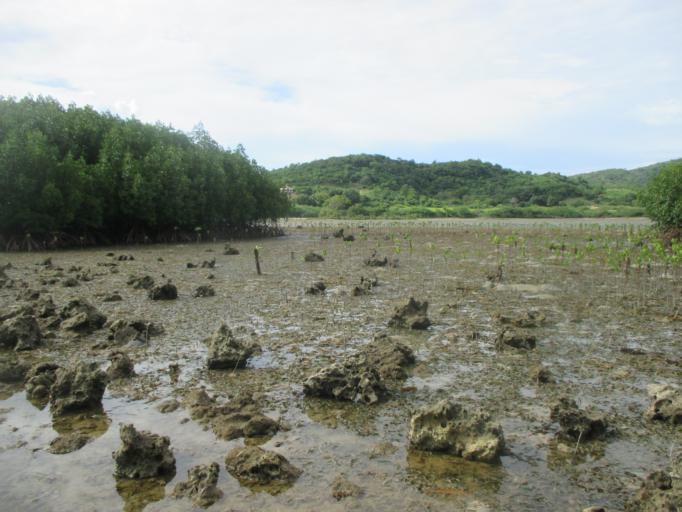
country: PH
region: Calabarzon
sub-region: Province of Batangas
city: Prinza
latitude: 14.0040
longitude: 120.6204
